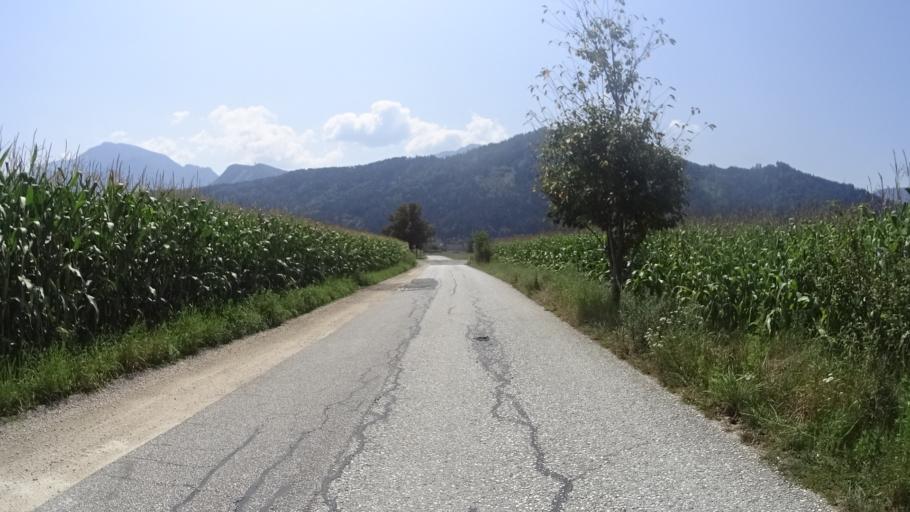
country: AT
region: Carinthia
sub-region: Politischer Bezirk Volkermarkt
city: Globasnitz
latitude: 46.5659
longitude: 14.6685
